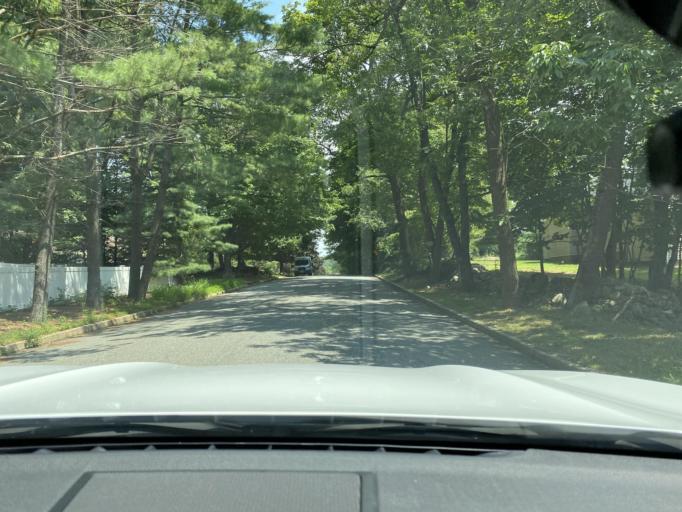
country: US
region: New York
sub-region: Rockland County
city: Airmont
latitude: 41.0891
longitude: -74.1255
